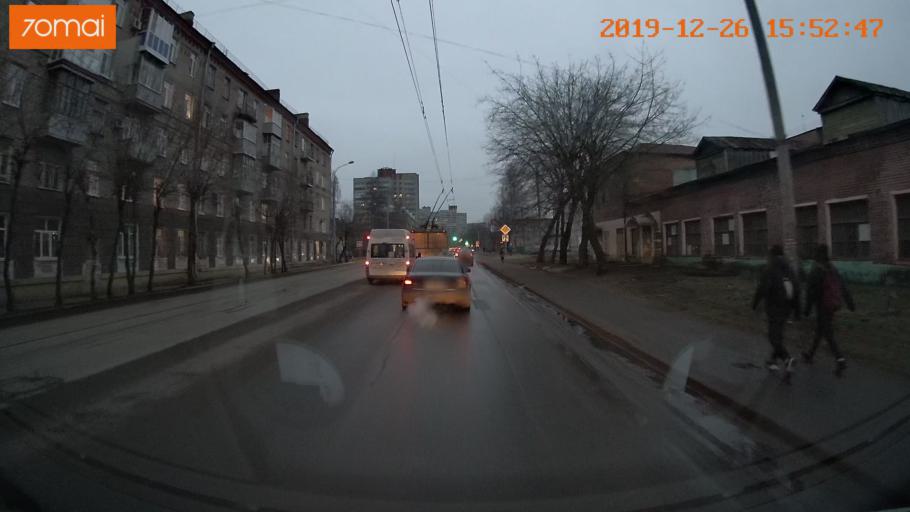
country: RU
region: Jaroslavl
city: Rybinsk
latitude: 58.0505
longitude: 38.8243
